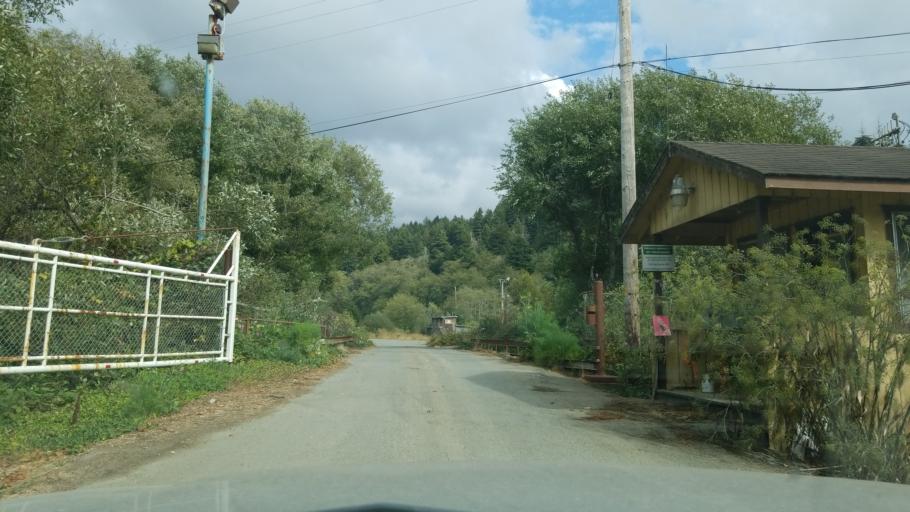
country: US
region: California
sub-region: Del Norte County
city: Bertsch-Oceanview
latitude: 41.5244
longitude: -124.0297
